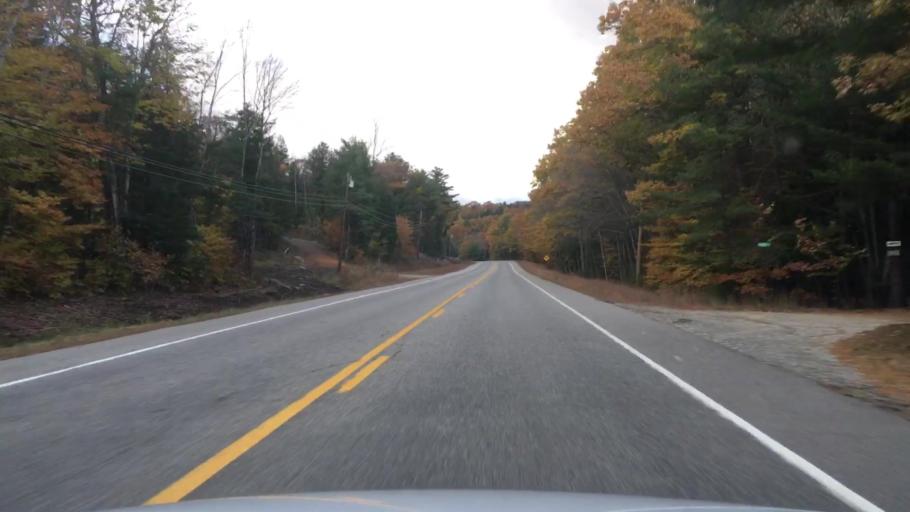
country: US
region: Maine
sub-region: Androscoggin County
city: Livermore
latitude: 44.3945
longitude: -70.2565
